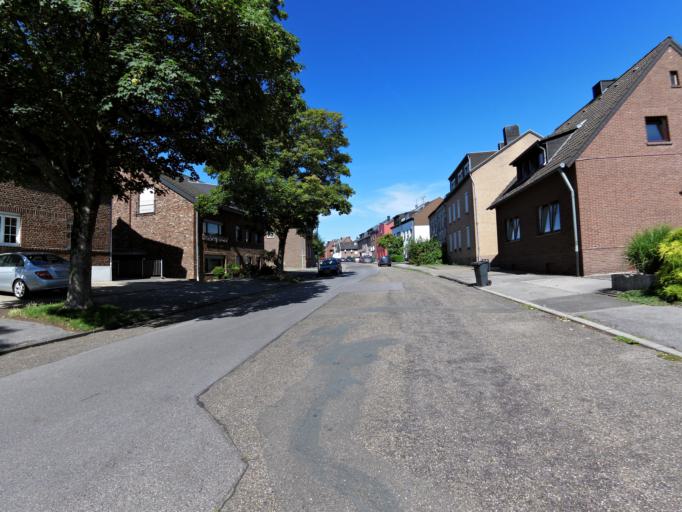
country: DE
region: North Rhine-Westphalia
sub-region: Regierungsbezirk Koln
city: Herzogenrath
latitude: 50.8427
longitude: 6.0908
